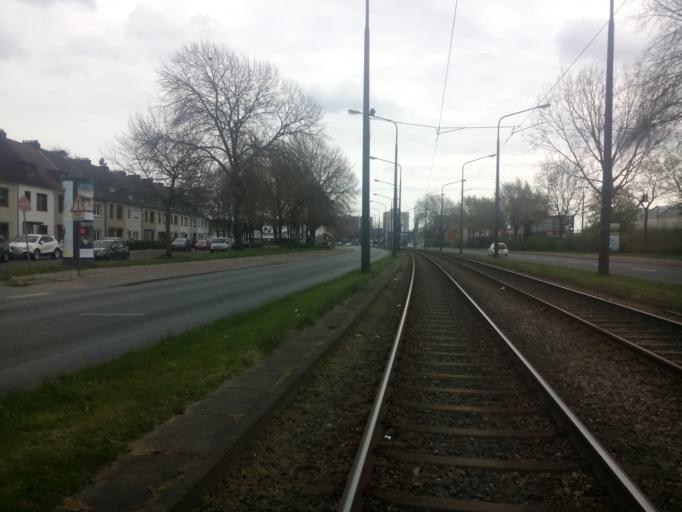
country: DE
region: Bremen
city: Bremen
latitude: 53.0909
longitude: 8.7823
